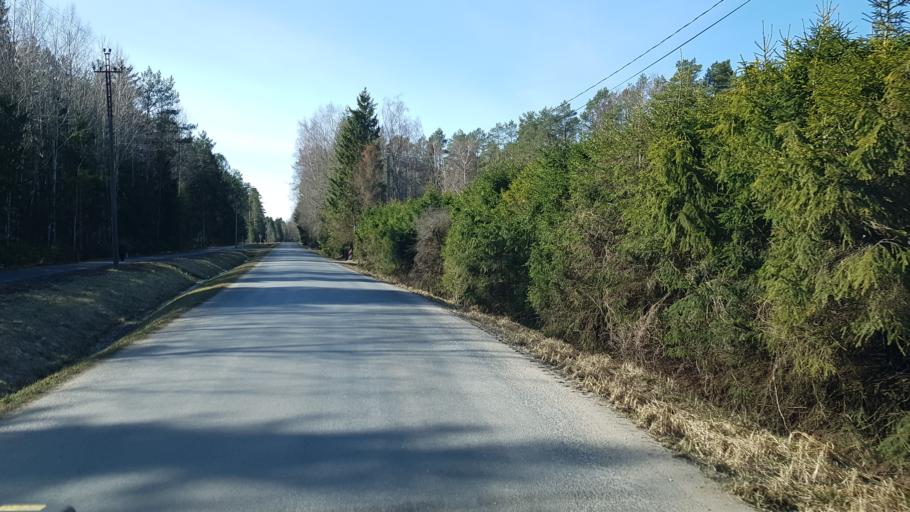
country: EE
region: Harju
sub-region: Saku vald
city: Saku
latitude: 59.2640
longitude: 24.6621
